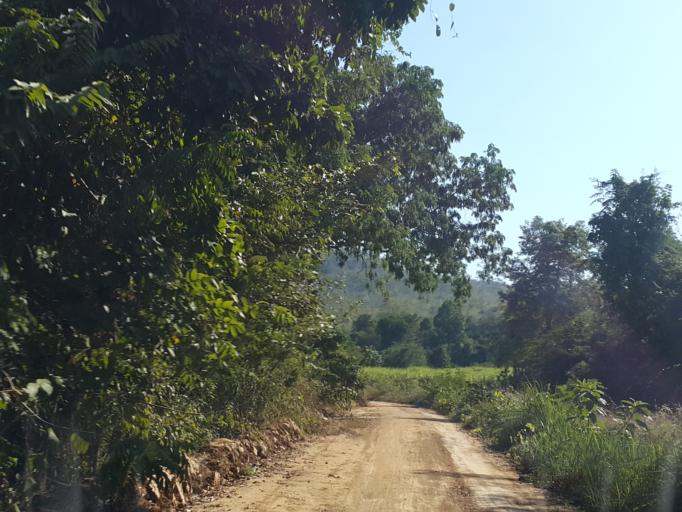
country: TH
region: Sukhothai
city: Thung Saliam
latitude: 17.3152
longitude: 99.4456
